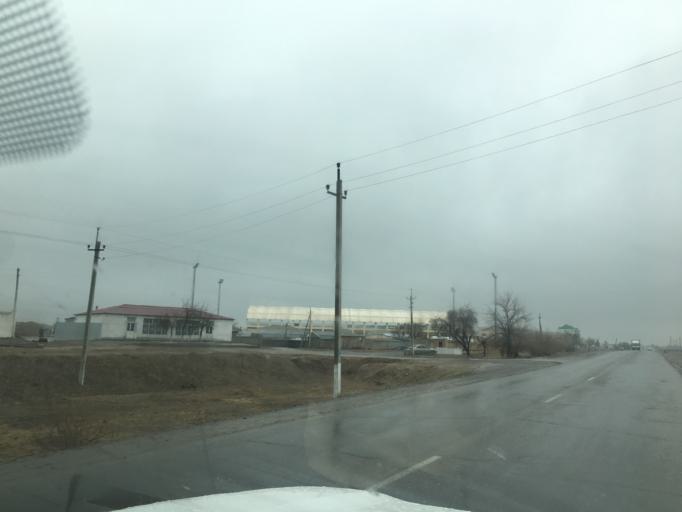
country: TM
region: Mary
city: Yoloeten
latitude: 37.2924
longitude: 62.3381
